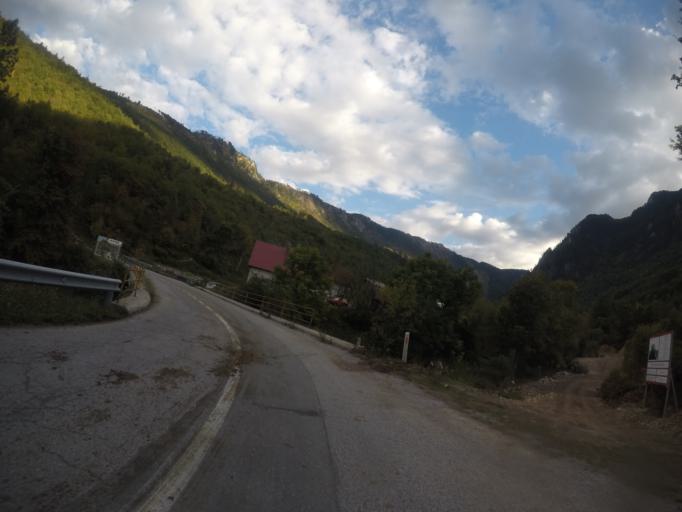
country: ME
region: Mojkovac
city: Mojkovac
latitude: 42.9879
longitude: 19.4340
